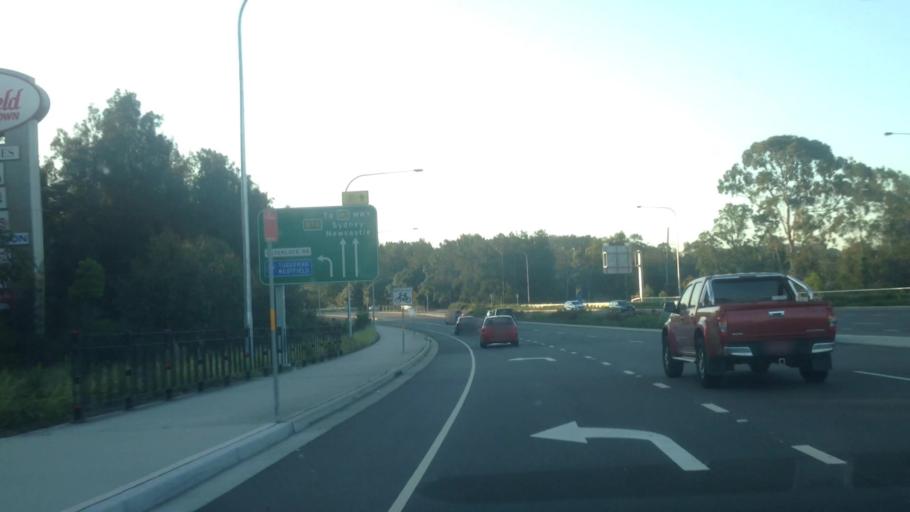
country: AU
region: New South Wales
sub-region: Wyong Shire
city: Chittaway Bay
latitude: -33.3082
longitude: 151.4177
